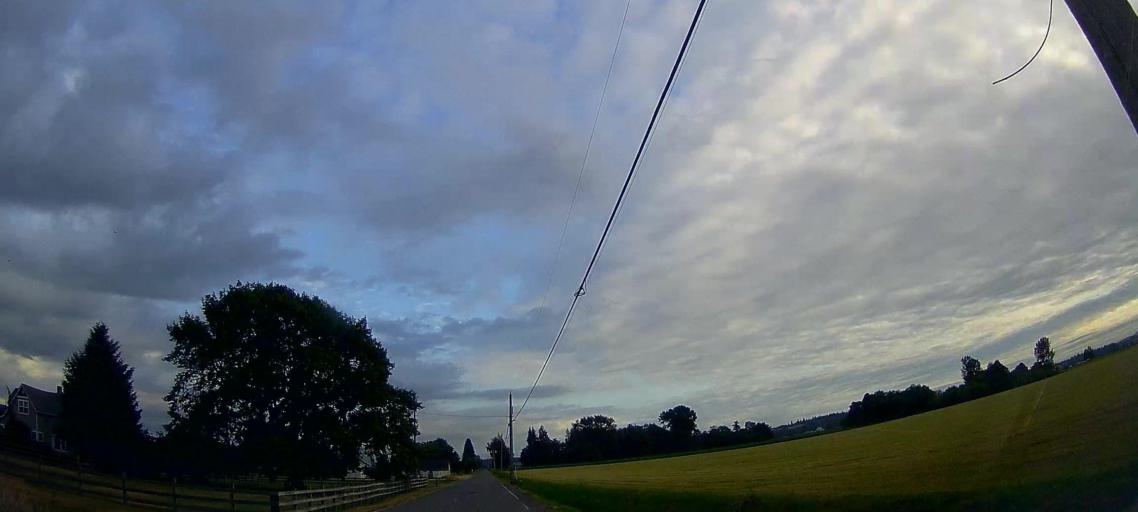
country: US
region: Washington
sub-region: Skagit County
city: Burlington
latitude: 48.5367
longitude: -122.4114
